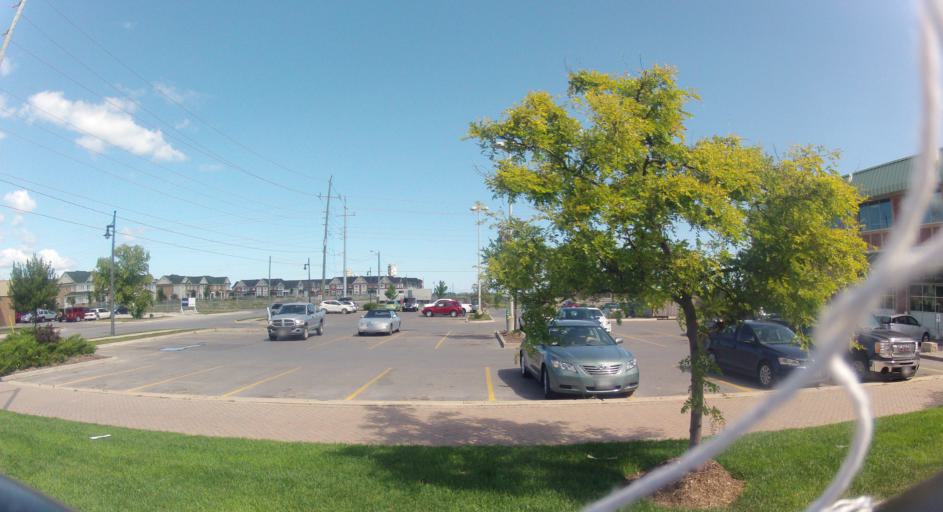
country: CA
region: Ontario
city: Collingwood
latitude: 44.5028
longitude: -80.2187
